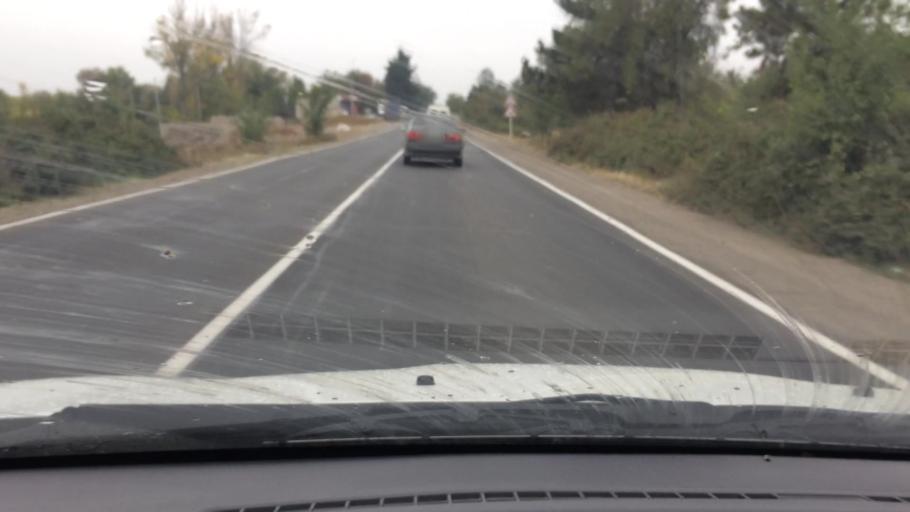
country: GE
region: Kvemo Kartli
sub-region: Marneuli
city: Marneuli
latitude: 41.4109
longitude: 44.8307
